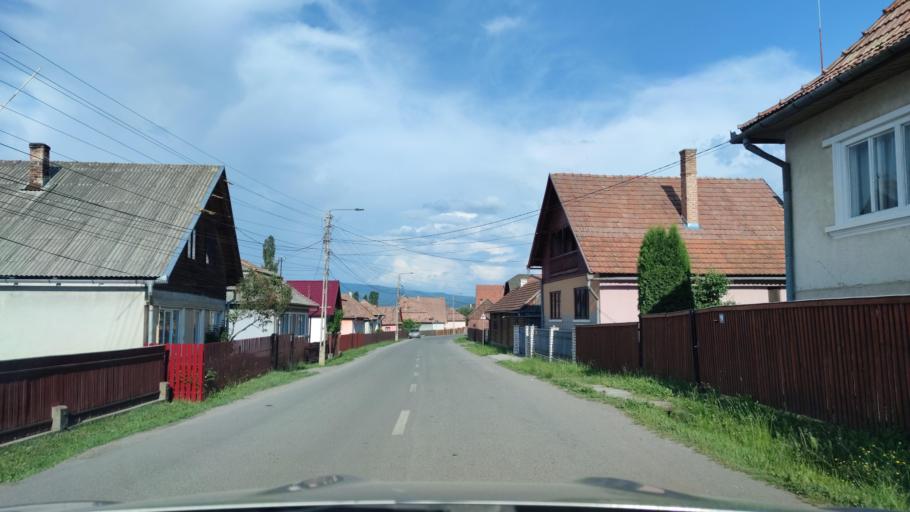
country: RO
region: Harghita
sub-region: Comuna Remetea
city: Remetea
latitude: 46.7939
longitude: 25.4417
